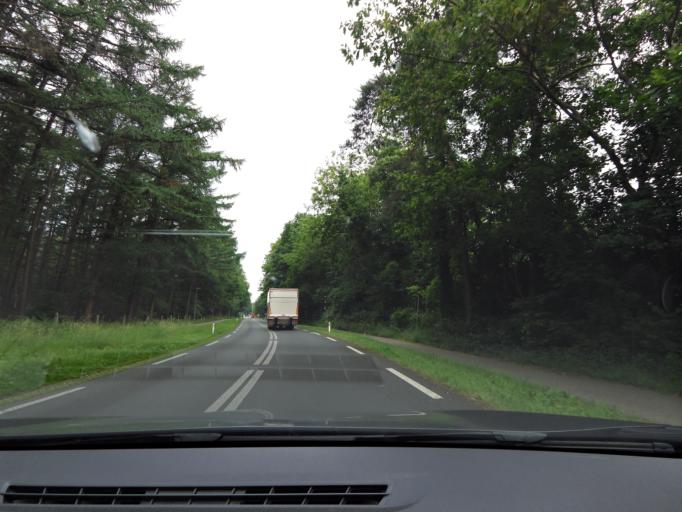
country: NL
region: Gelderland
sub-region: Gemeente Brummen
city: Eerbeek
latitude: 52.0921
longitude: 6.0624
